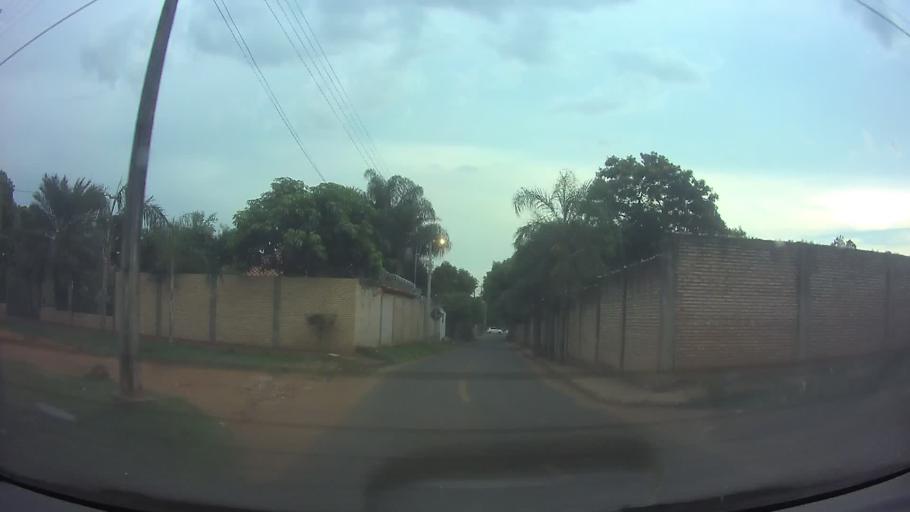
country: PY
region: Central
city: San Lorenzo
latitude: -25.2806
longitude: -57.4817
